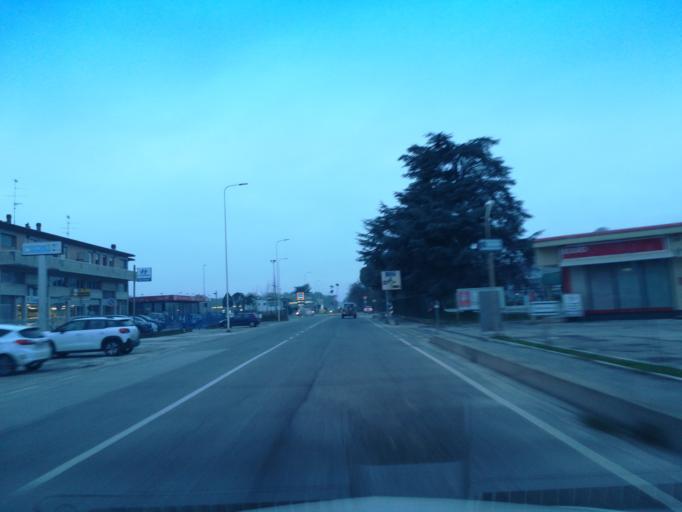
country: IT
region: Emilia-Romagna
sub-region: Provincia di Ravenna
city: Faenza
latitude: 44.2942
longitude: 11.8626
